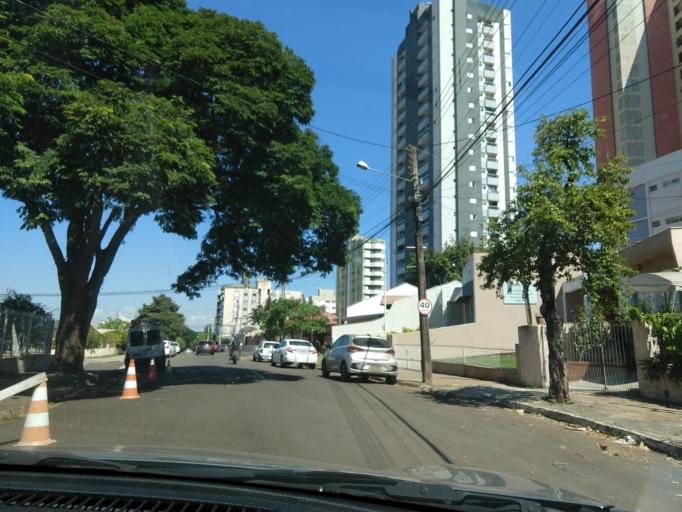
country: BR
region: Parana
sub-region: Londrina
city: Londrina
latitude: -23.3269
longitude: -51.1666
